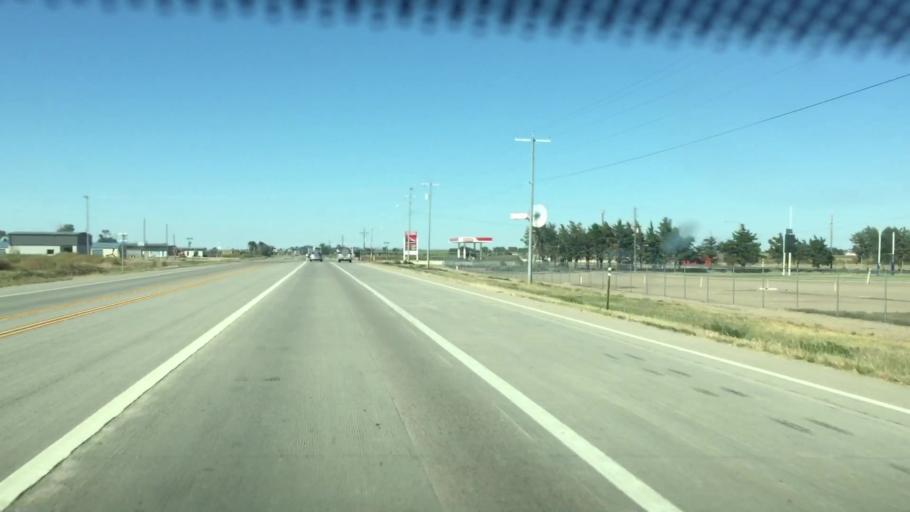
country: US
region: Colorado
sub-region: Prowers County
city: Lamar
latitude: 38.1564
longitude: -102.7236
